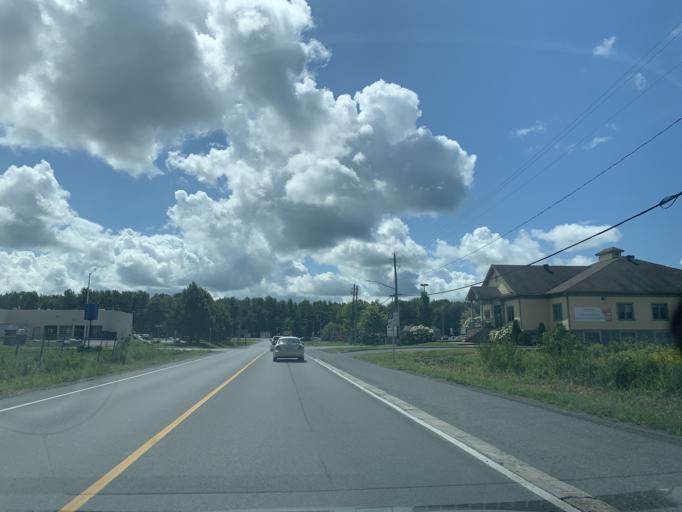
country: CA
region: Ontario
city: Hawkesbury
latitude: 45.5941
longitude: -74.5997
